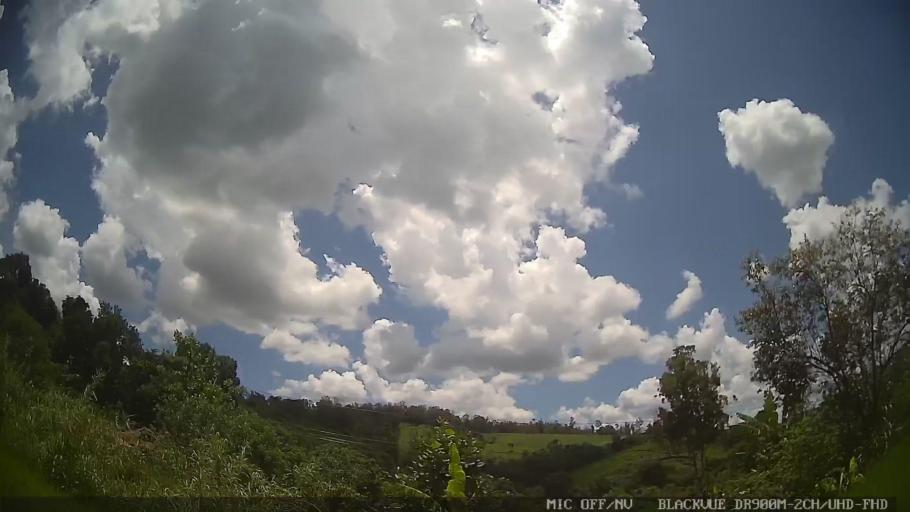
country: BR
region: Sao Paulo
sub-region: Amparo
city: Amparo
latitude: -22.6813
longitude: -46.7415
